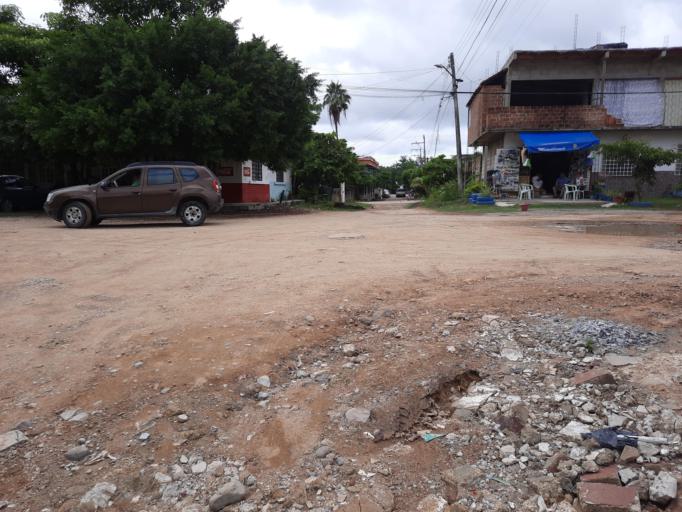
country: MX
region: Jalisco
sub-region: Puerto Vallarta
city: Puerto Vallarta
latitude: 20.6588
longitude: -105.2105
